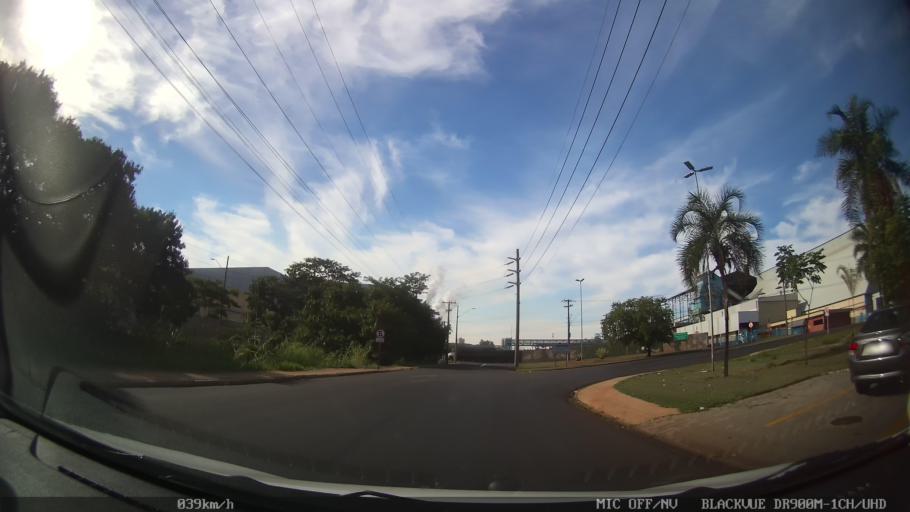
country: BR
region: Sao Paulo
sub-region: Araraquara
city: Araraquara
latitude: -21.8044
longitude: -48.1713
